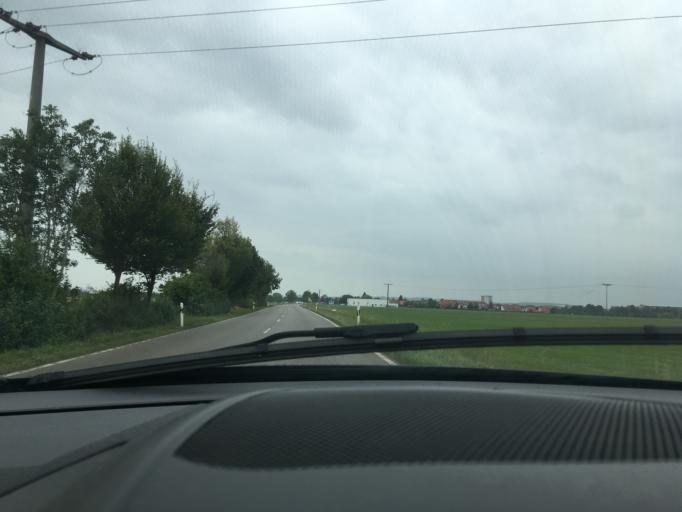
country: DE
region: Baden-Wuerttemberg
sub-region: Tuebingen Region
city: Kirchdorf
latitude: 48.0643
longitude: 10.1253
